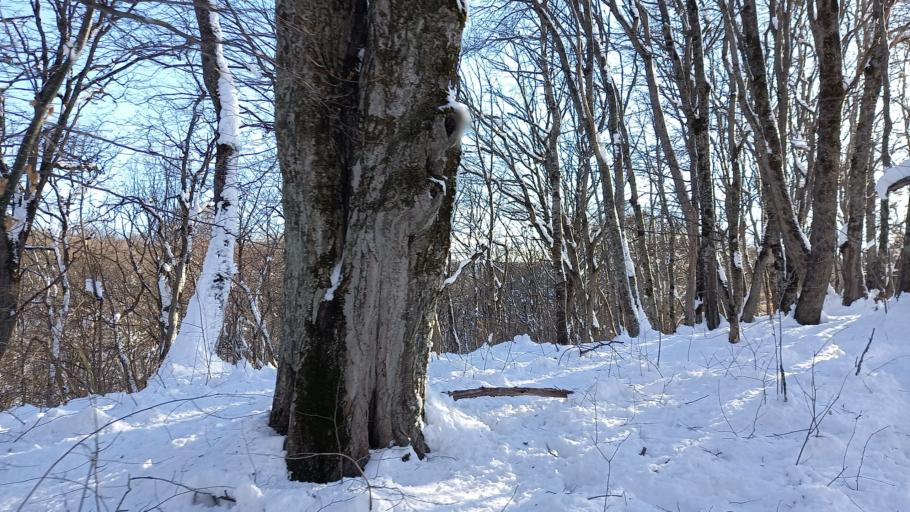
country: RU
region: Krasnodarskiy
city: Gubskaya
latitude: 44.3103
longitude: 40.4403
